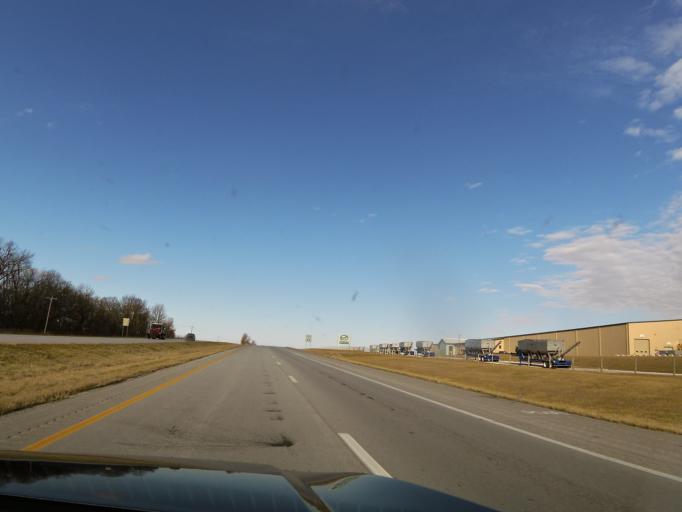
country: US
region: Missouri
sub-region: Marion County
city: Palmyra
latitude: 39.8530
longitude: -91.5251
